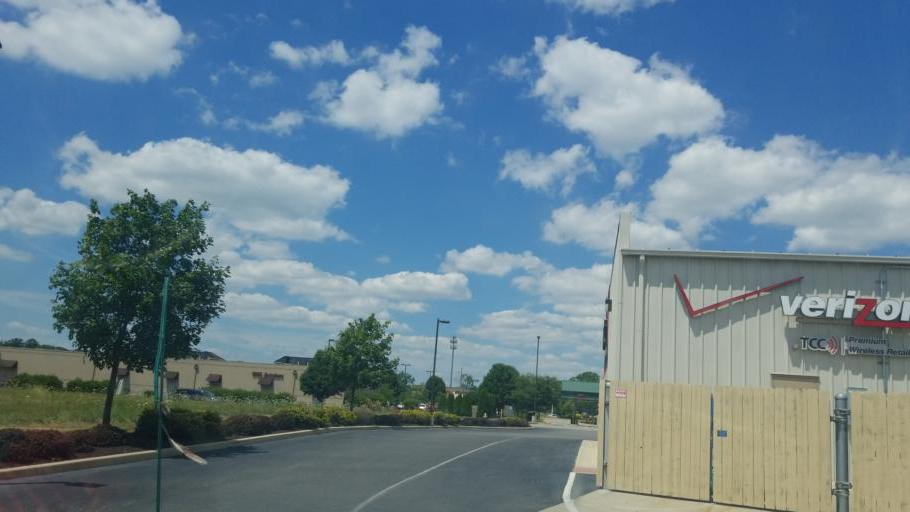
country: US
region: Indiana
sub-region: Allen County
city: New Haven
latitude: 41.1280
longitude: -85.0108
